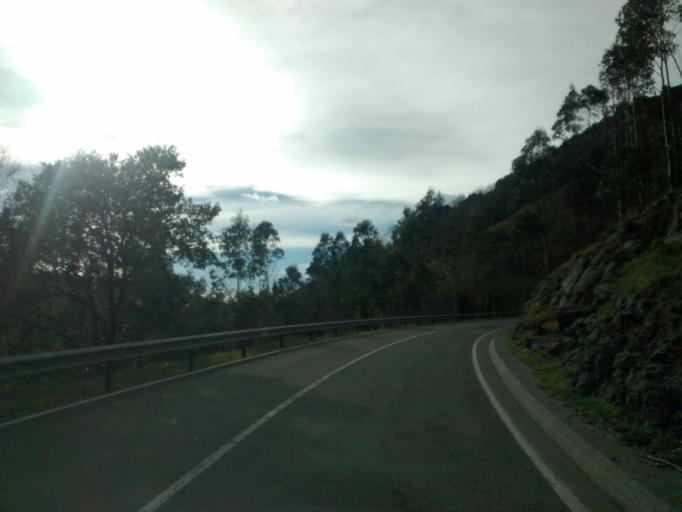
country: ES
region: Cantabria
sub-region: Provincia de Cantabria
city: Arredondo
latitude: 43.2798
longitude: -3.6149
